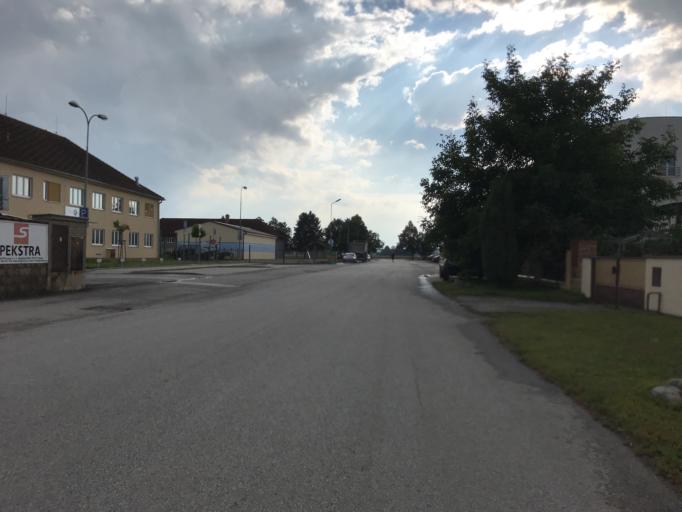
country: CZ
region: Jihocesky
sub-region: Okres Jindrichuv Hradec
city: Trebon
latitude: 49.0175
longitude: 14.7579
